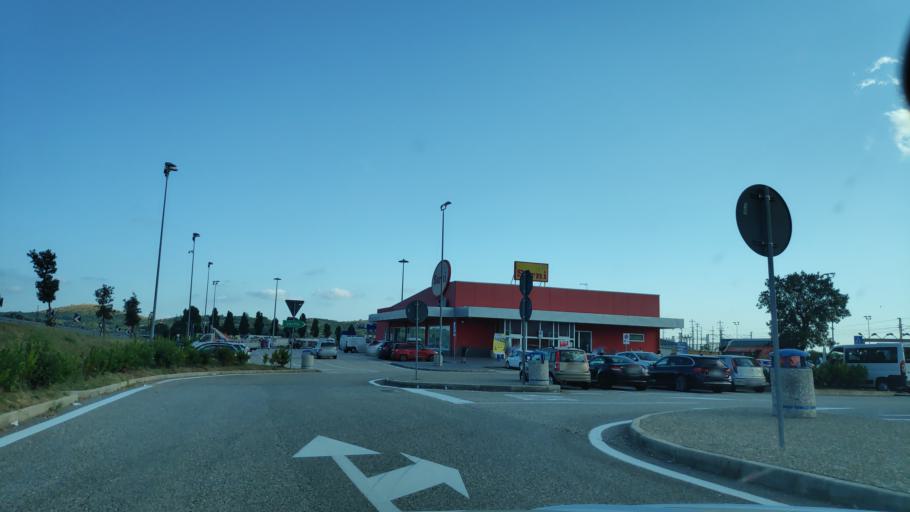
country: IT
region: Campania
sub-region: Provincia di Caserta
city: Teano
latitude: 41.2342
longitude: 14.0923
